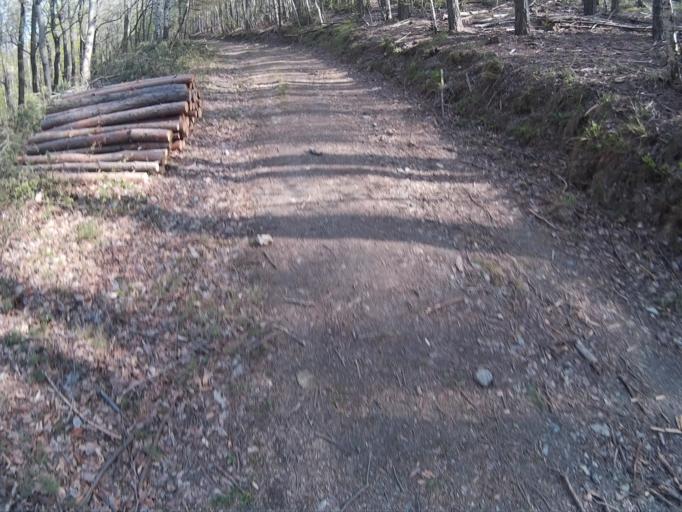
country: AT
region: Burgenland
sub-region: Politischer Bezirk Oberwart
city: Rechnitz
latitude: 47.3370
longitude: 16.4617
